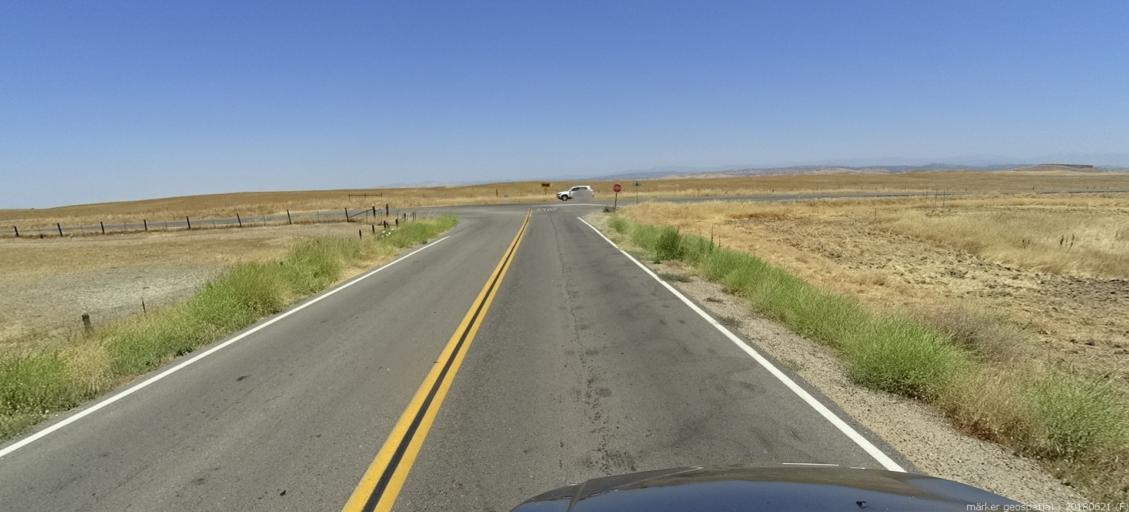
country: US
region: California
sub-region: Madera County
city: Bonadelle Ranchos-Madera Ranchos
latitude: 37.0097
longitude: -119.8937
